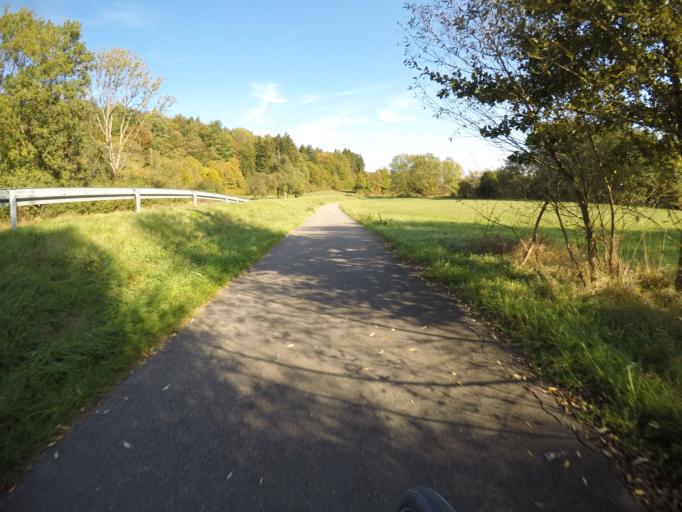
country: DE
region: Baden-Wuerttemberg
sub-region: Regierungsbezirk Stuttgart
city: Schlaitdorf
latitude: 48.6288
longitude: 9.1950
